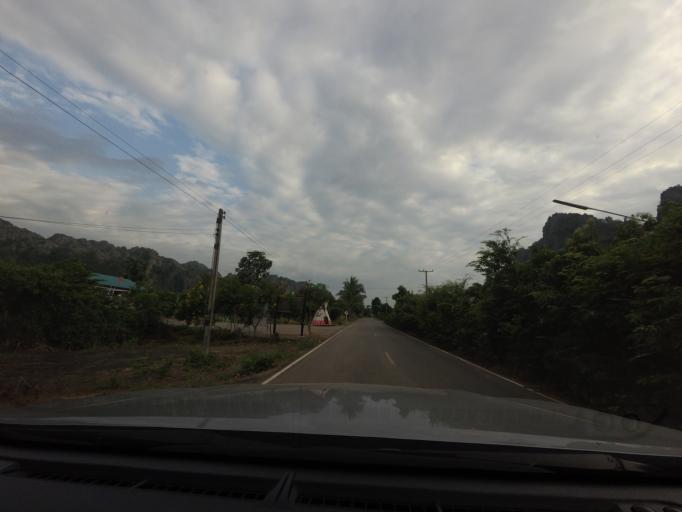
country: TH
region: Phitsanulok
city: Noen Maprang
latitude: 16.5749
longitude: 100.6842
